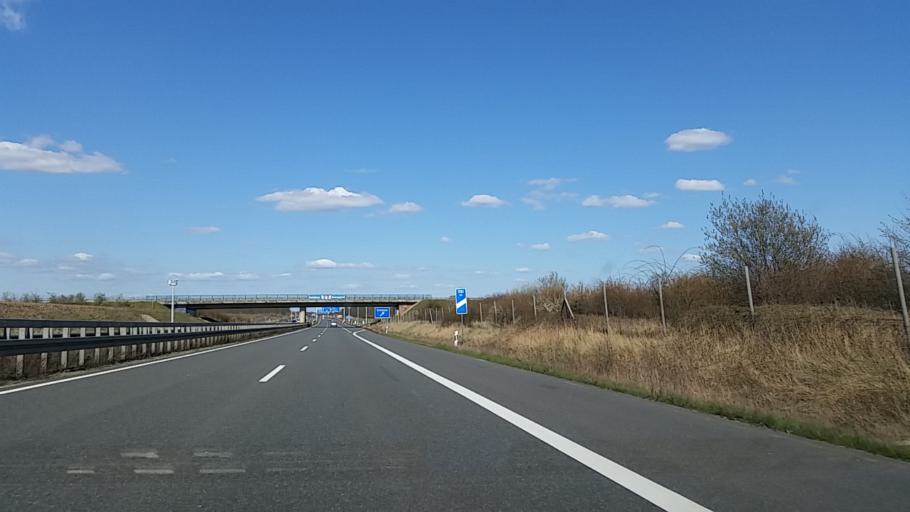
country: DE
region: Lower Saxony
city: Lehre
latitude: 52.2945
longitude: 10.7196
